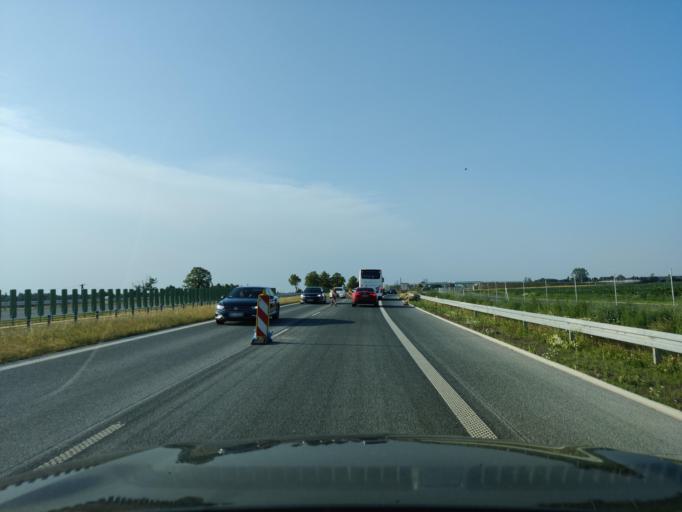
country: PL
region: Masovian Voivodeship
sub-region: Powiat plonski
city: Plonsk
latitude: 52.6429
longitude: 20.3737
